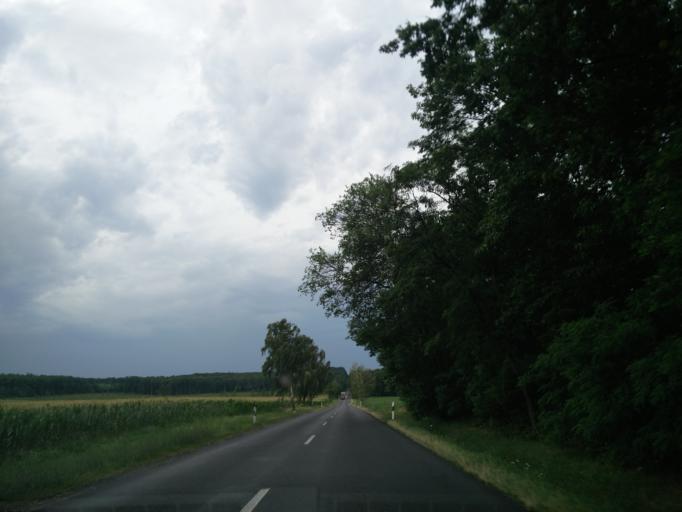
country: HU
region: Vas
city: Vasvar
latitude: 47.0167
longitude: 16.8229
